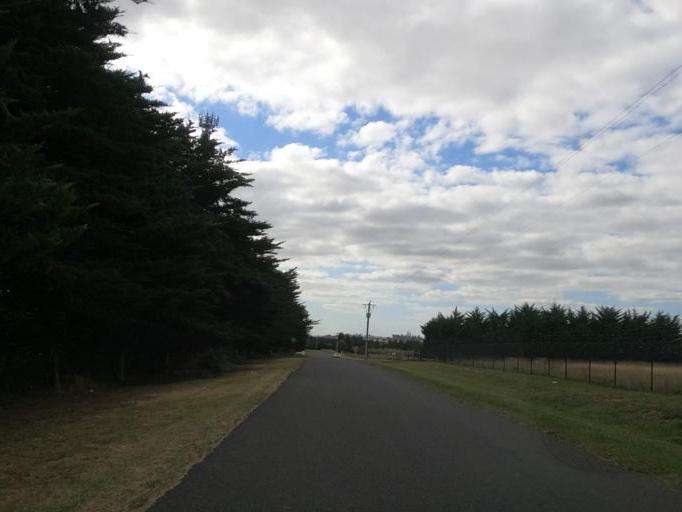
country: AU
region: Victoria
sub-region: Hume
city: Greenvale
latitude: -37.5591
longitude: 144.8699
